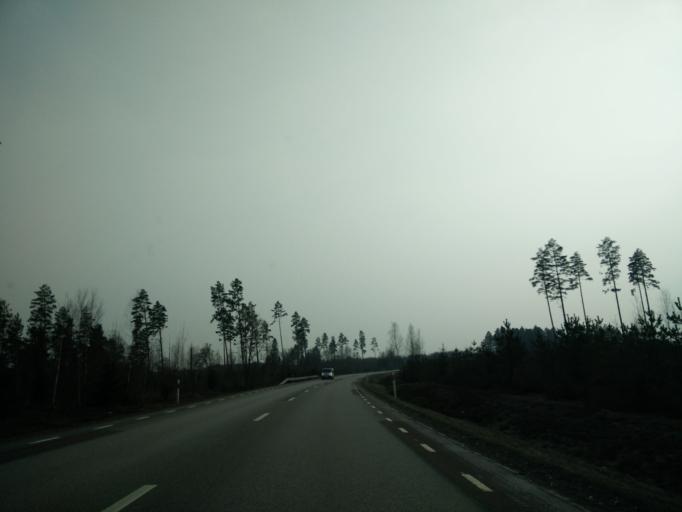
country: SE
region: Vaermland
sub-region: Forshaga Kommun
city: Forshaga
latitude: 59.4996
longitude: 13.4332
